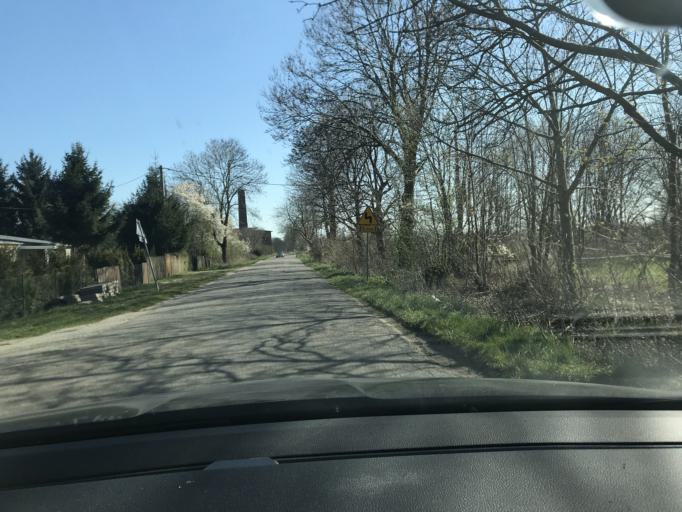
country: PL
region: Pomeranian Voivodeship
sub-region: Powiat nowodworski
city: Sztutowo
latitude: 54.3183
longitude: 19.1589
